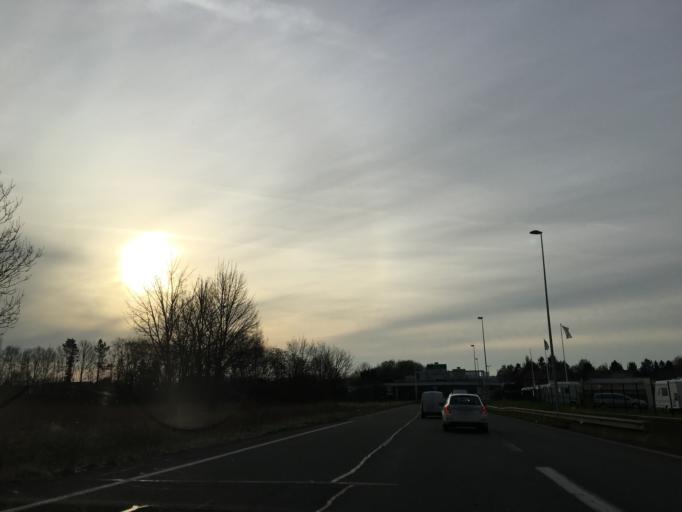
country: FR
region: Nord-Pas-de-Calais
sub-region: Departement du Pas-de-Calais
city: Saint-Nicolas
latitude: 50.3060
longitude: 2.7841
